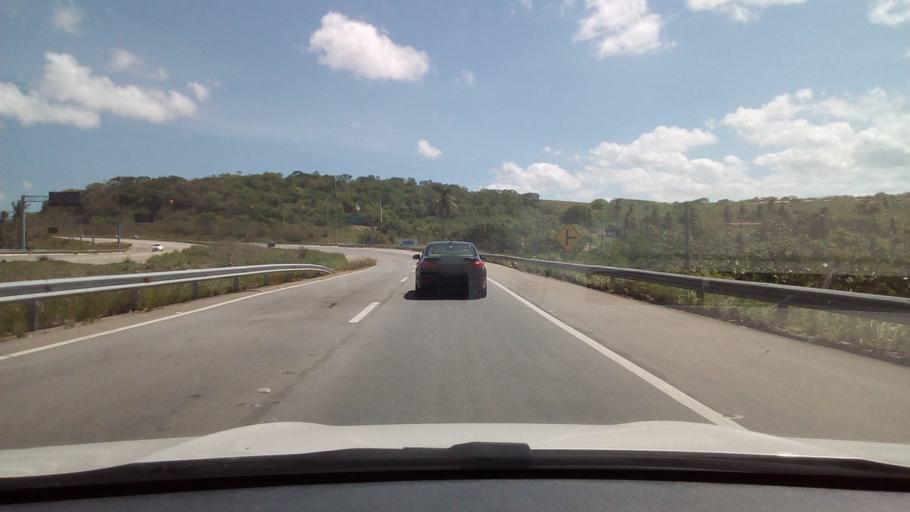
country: BR
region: Rio Grande do Norte
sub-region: Nisia Floresta
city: Nisia Floresta
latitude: -6.1129
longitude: -35.2336
